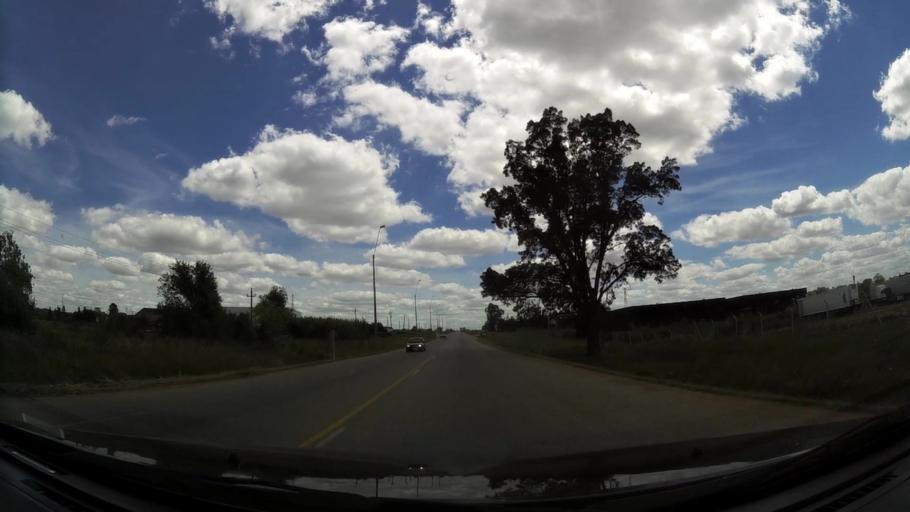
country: UY
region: Canelones
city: Colonia Nicolich
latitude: -34.7995
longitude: -56.0040
